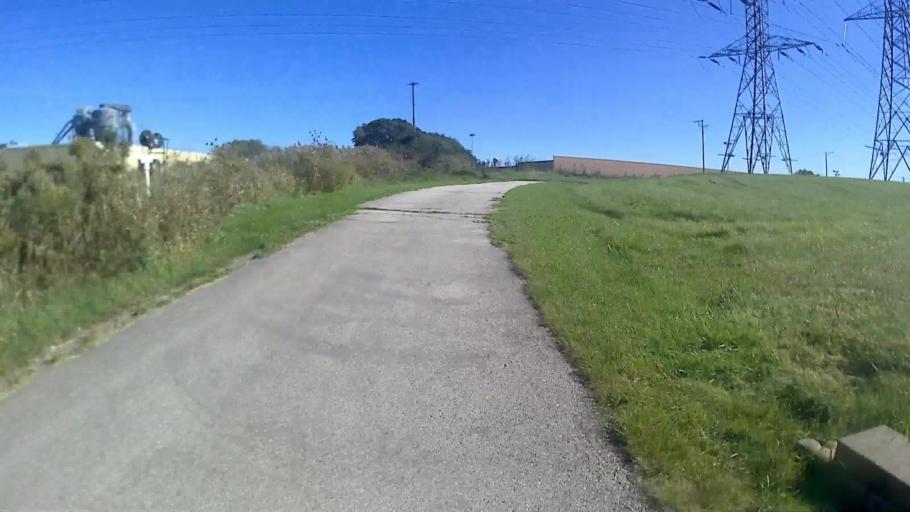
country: US
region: Illinois
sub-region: DuPage County
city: Itasca
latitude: 41.9687
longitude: -87.9945
